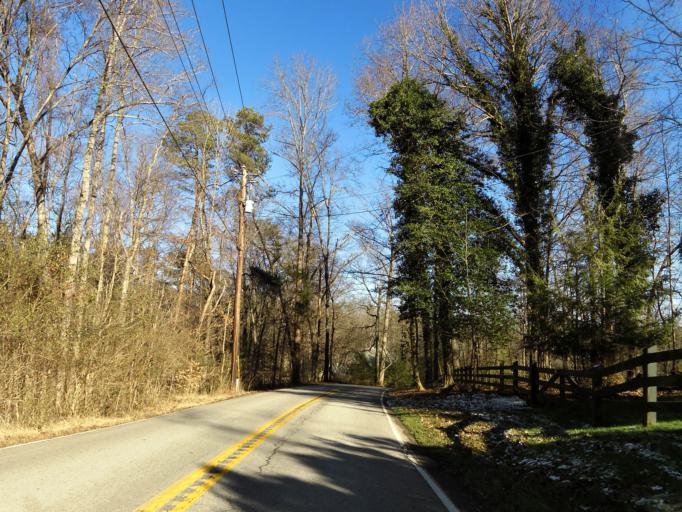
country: US
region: Tennessee
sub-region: Blount County
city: Louisville
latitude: 35.8910
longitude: -83.9955
